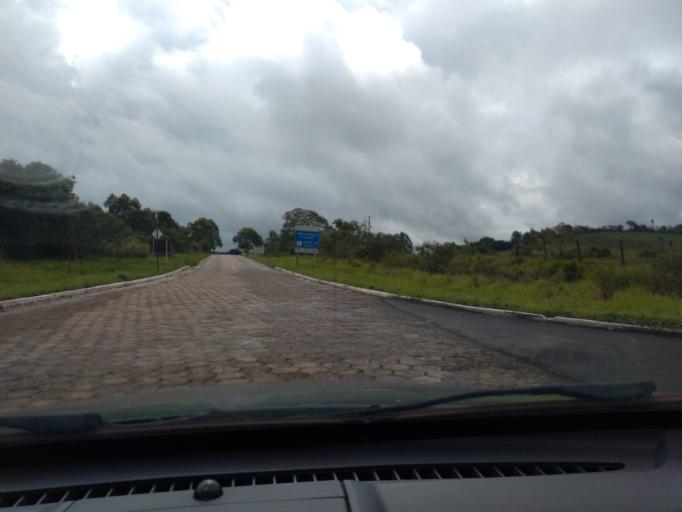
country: BR
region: Minas Gerais
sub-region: Lavras
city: Lavras
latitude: -21.5061
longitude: -44.9168
